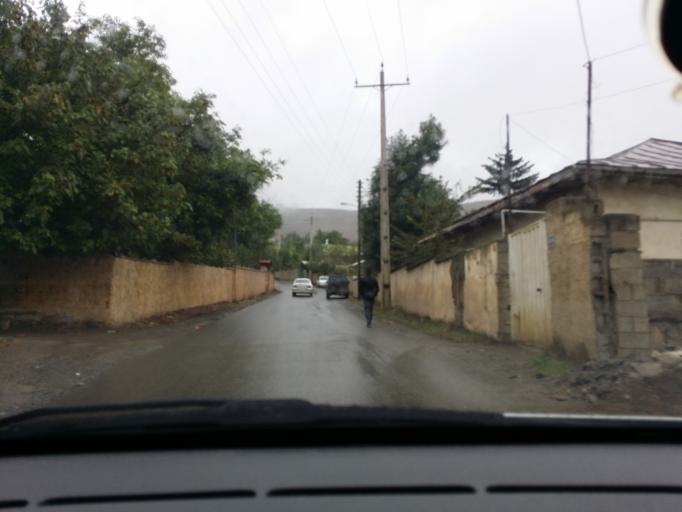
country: IR
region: Mazandaran
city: Chalus
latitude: 36.5281
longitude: 51.2284
